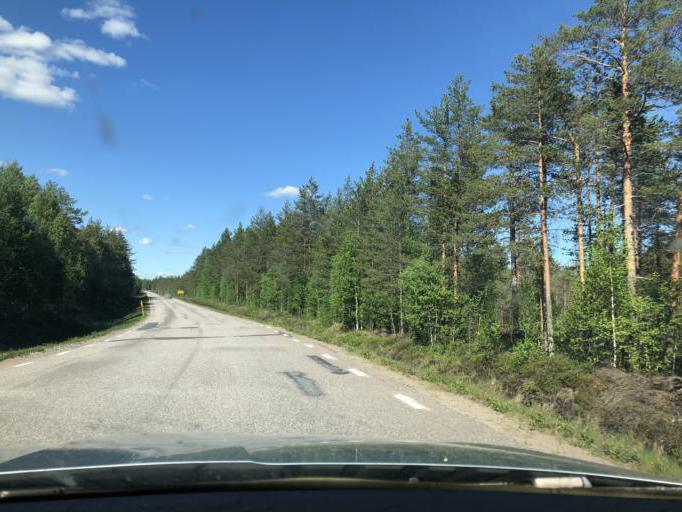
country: SE
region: Norrbotten
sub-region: Kalix Kommun
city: Kalix
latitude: 65.8995
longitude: 23.1684
